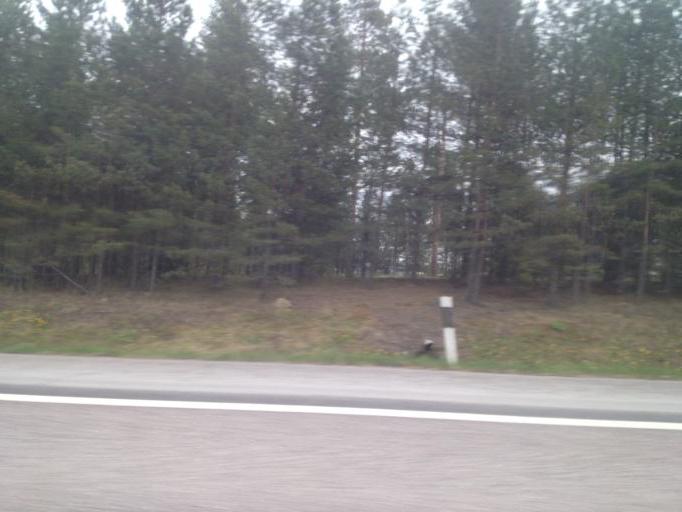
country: FI
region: Uusimaa
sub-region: Helsinki
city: Nurmijaervi
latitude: 60.4928
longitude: 24.8516
